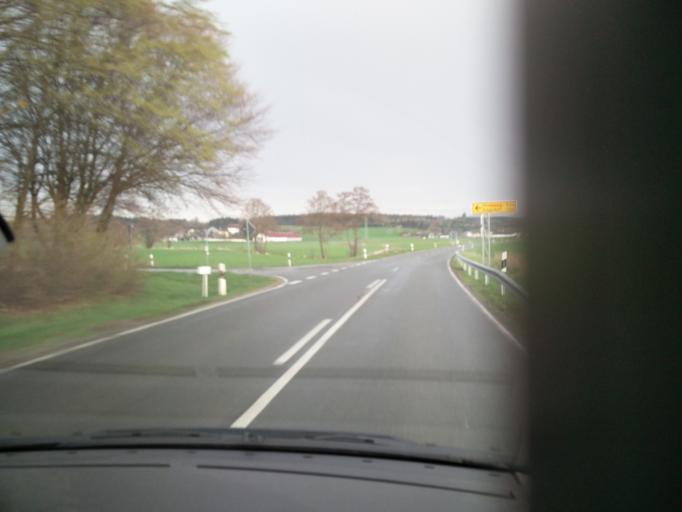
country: DE
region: Bavaria
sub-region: Upper Bavaria
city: Bad Endorf
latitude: 47.9268
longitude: 12.2893
